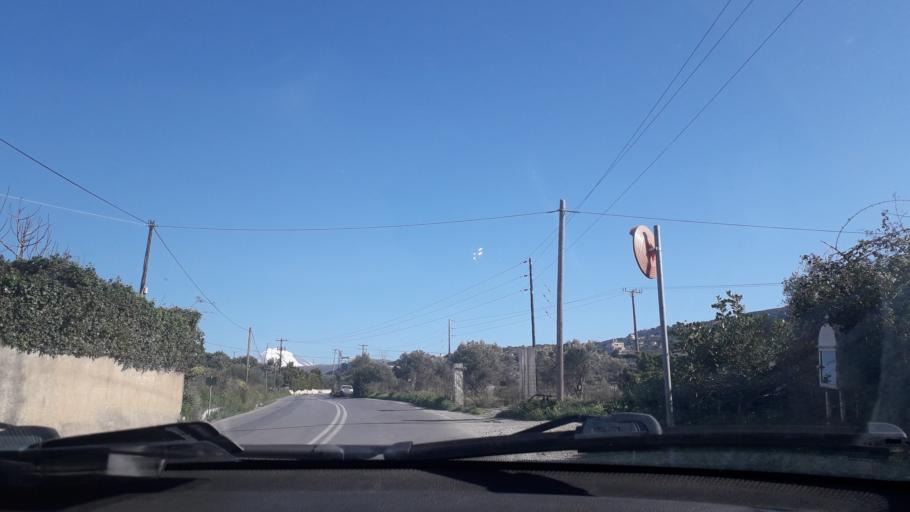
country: GR
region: Crete
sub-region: Nomos Rethymnis
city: Rethymno
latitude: 35.3634
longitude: 24.5419
